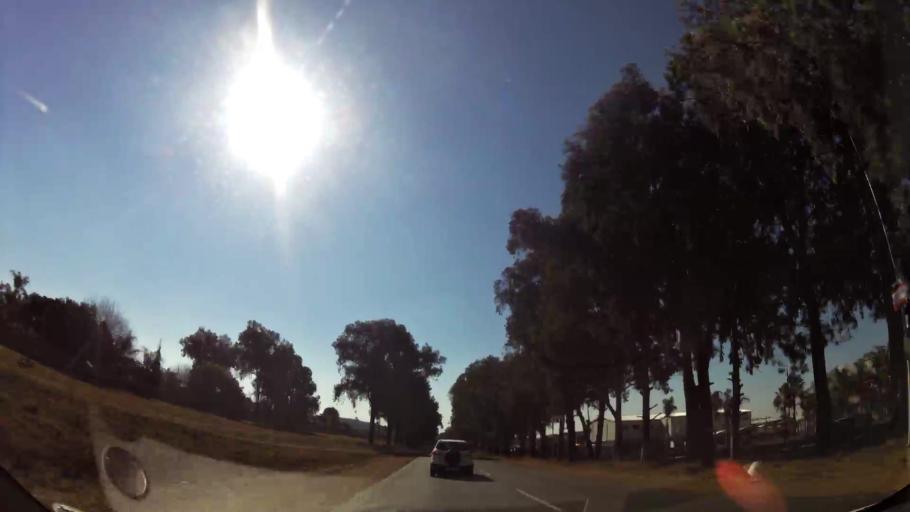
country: ZA
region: Gauteng
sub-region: City of Tshwane Metropolitan Municipality
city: Centurion
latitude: -25.8682
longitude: 28.1625
